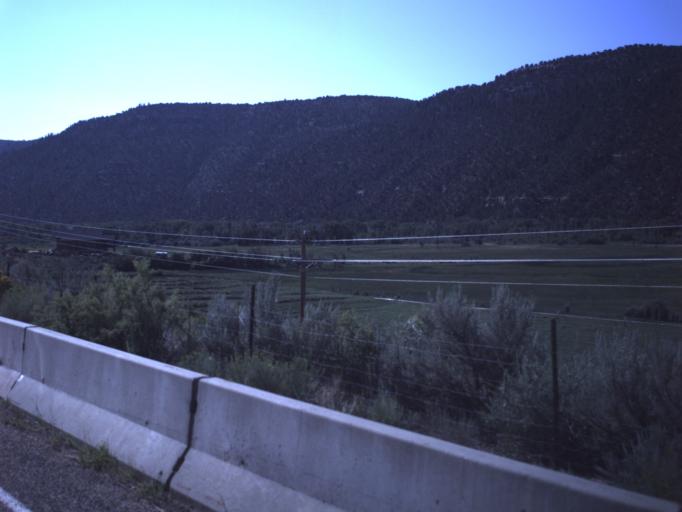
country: US
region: Utah
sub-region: Duchesne County
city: Duchesne
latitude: 40.3132
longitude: -110.6414
